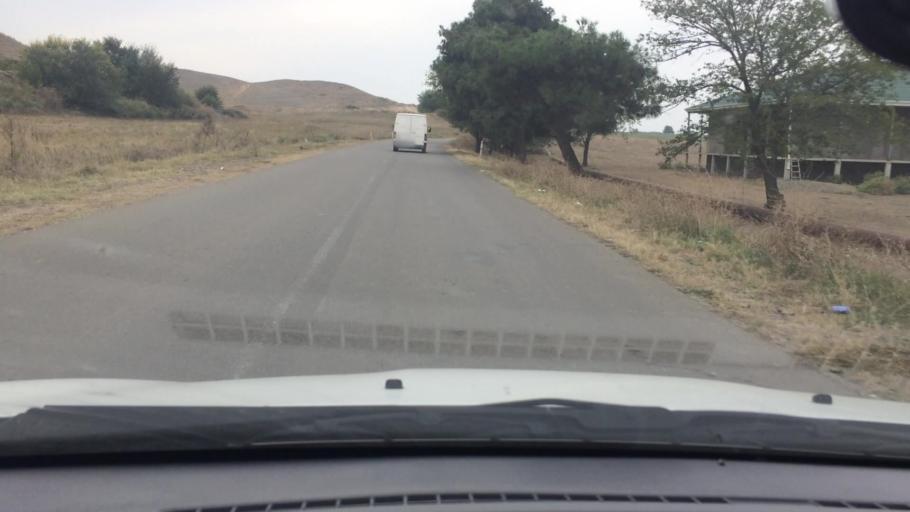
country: AM
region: Tavush
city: Berdavan
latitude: 41.3345
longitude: 45.0321
